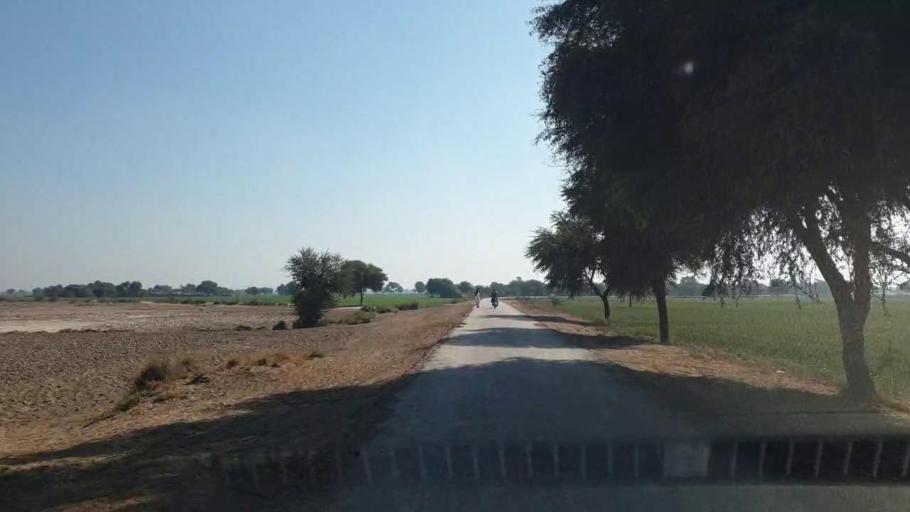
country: PK
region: Sindh
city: Shahpur Chakar
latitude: 26.1205
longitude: 68.6266
